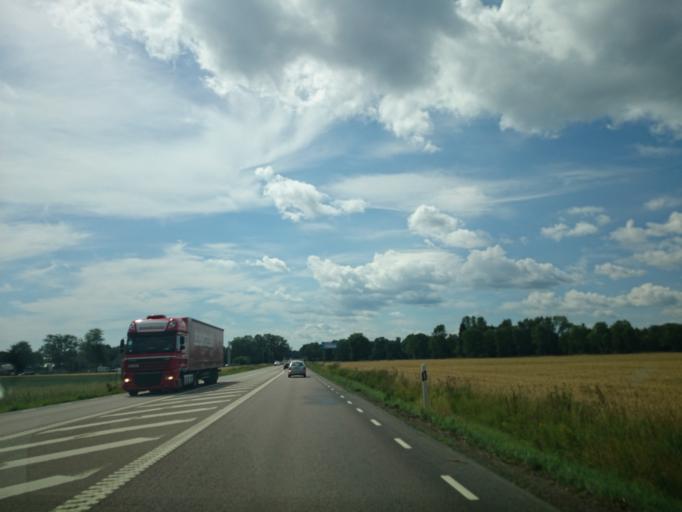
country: SE
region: Kalmar
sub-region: Monsteras Kommun
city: Moensteras
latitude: 57.0302
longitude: 16.4323
